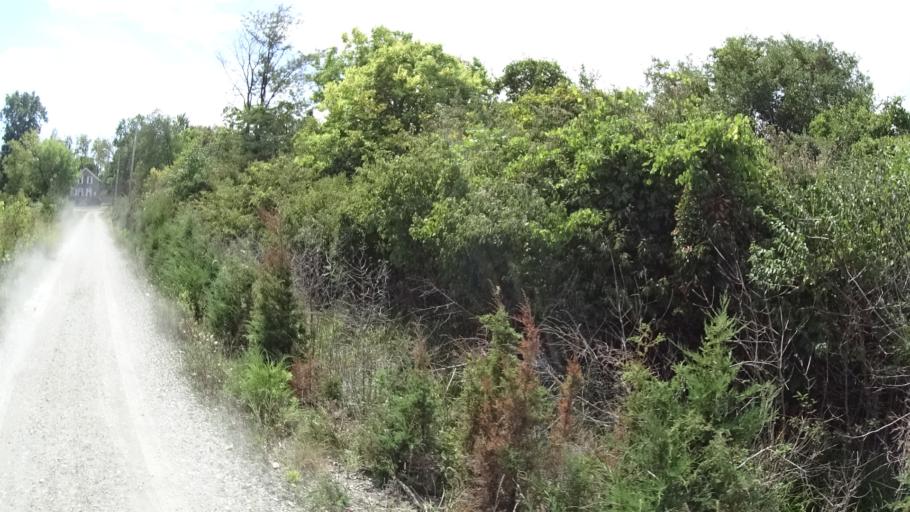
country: US
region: Ohio
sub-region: Erie County
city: Sandusky
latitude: 41.5963
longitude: -82.6837
